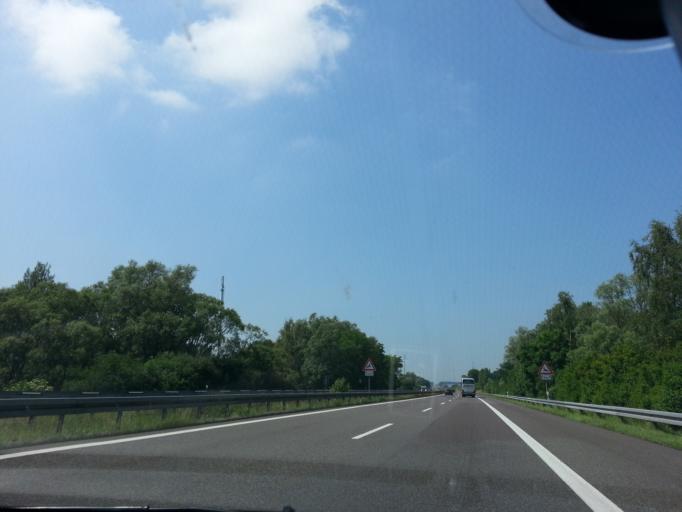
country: DE
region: Brandenburg
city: Gerdshagen
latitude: 53.2015
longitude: 12.2689
